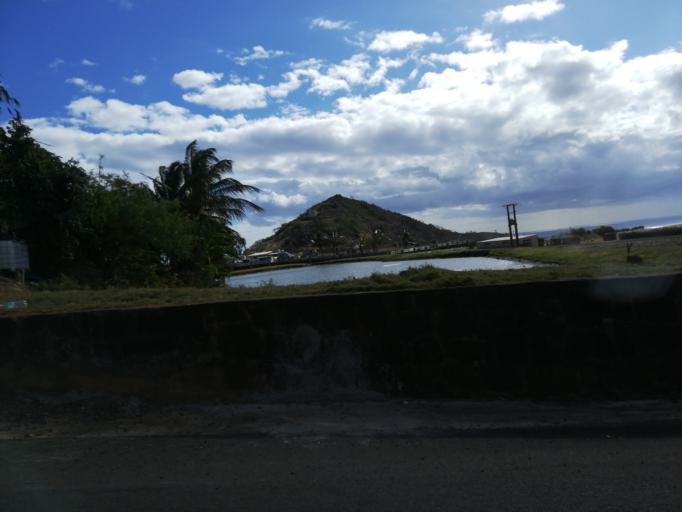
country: MU
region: Black River
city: Gros Cailloux
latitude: -20.2282
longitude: 57.4543
